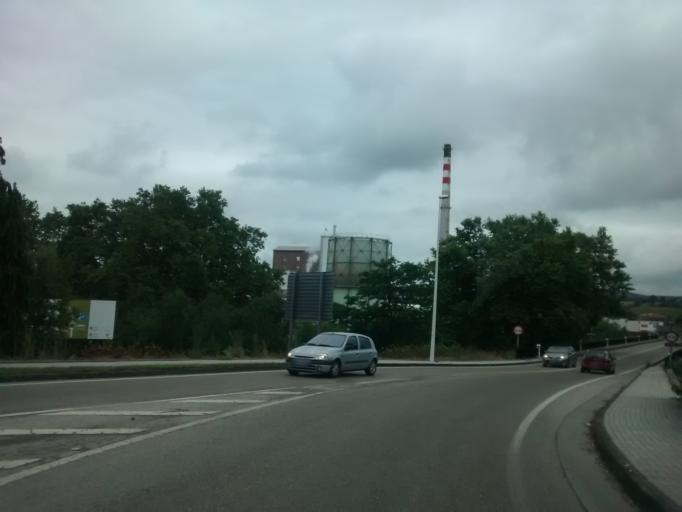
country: ES
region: Cantabria
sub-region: Provincia de Cantabria
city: Torrelavega
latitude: 43.3778
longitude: -4.0482
